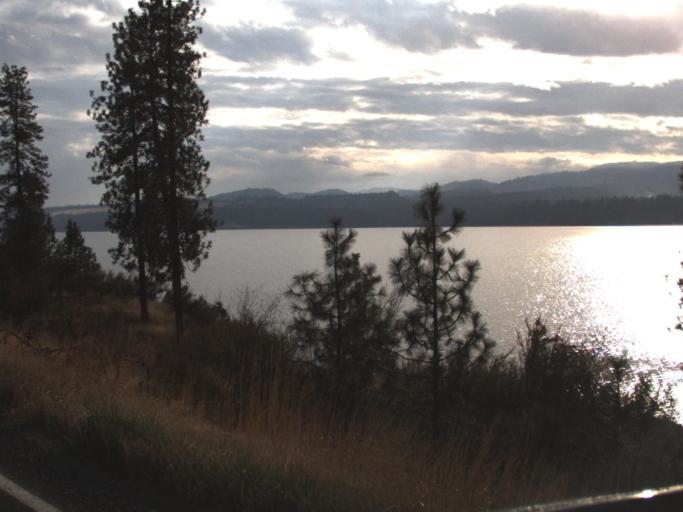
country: US
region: Washington
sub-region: Stevens County
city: Kettle Falls
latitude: 48.3275
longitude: -118.1532
